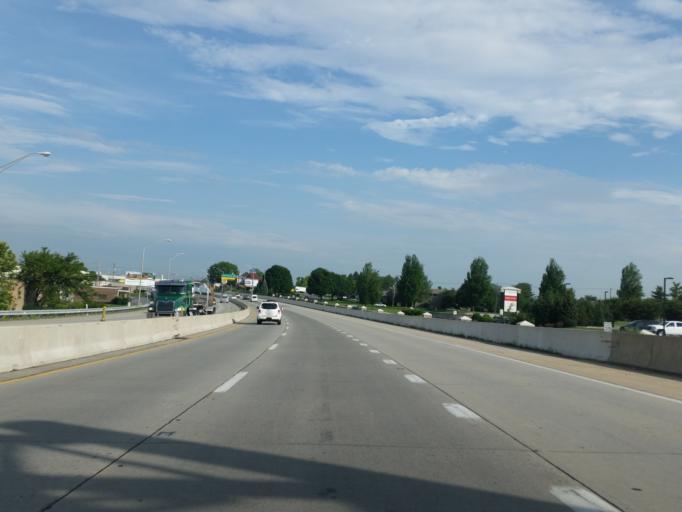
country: US
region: Pennsylvania
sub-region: Lancaster County
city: Lancaster
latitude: 40.0471
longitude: -76.2497
